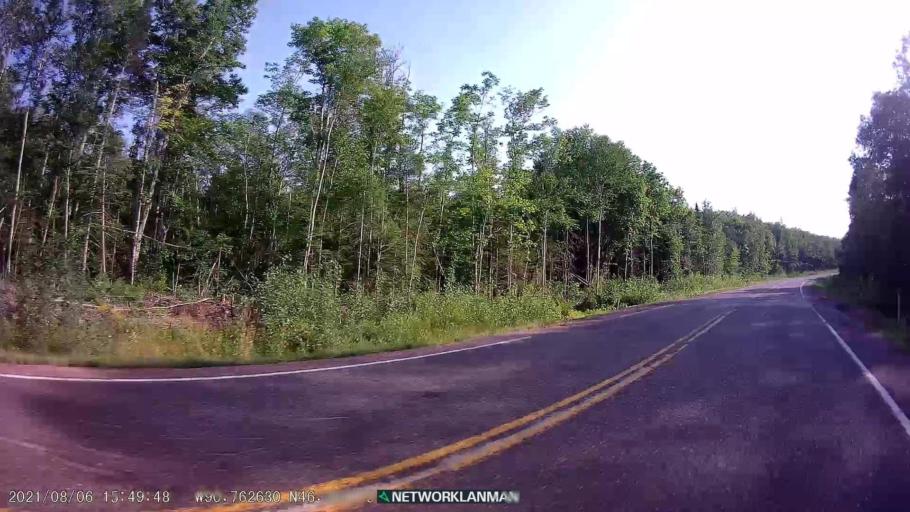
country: US
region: Wisconsin
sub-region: Ashland County
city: Ashland
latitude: 46.3040
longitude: -90.7629
